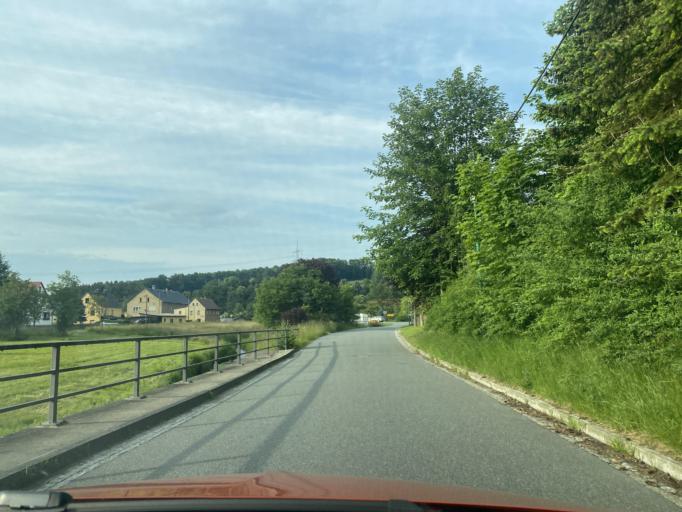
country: DE
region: Saxony
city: Bernstadt
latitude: 51.0277
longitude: 14.8009
